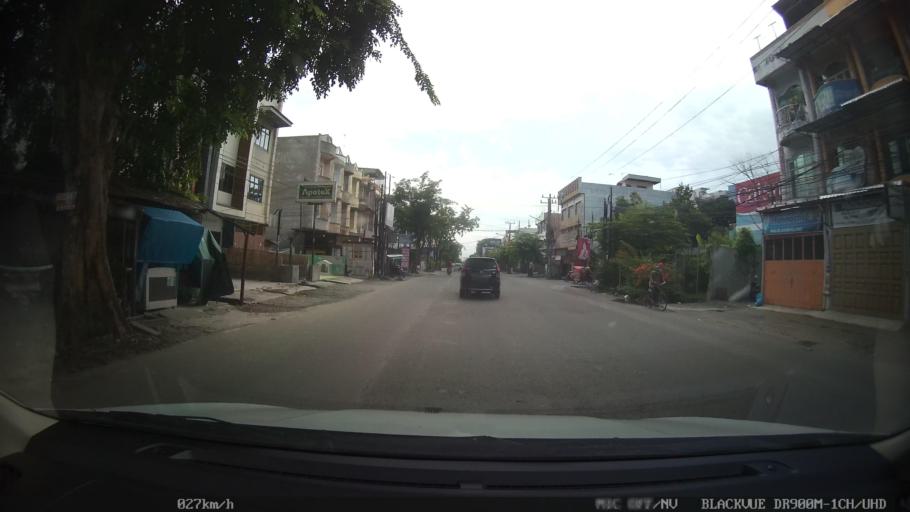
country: ID
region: North Sumatra
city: Medan
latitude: 3.6230
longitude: 98.6775
